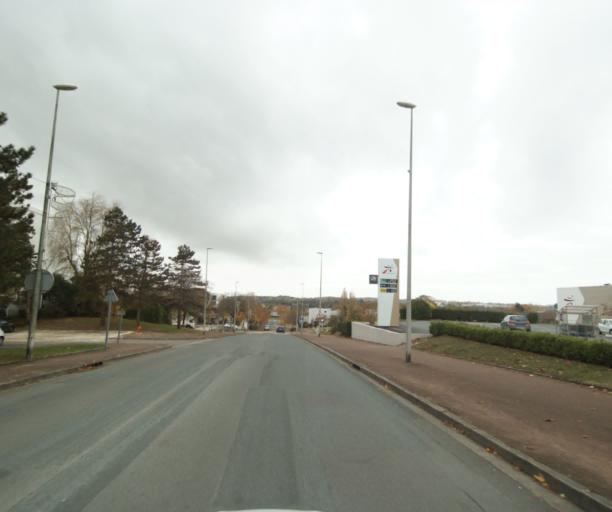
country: FR
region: Poitou-Charentes
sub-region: Departement de la Charente-Maritime
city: Saintes
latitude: 45.7358
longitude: -0.6494
